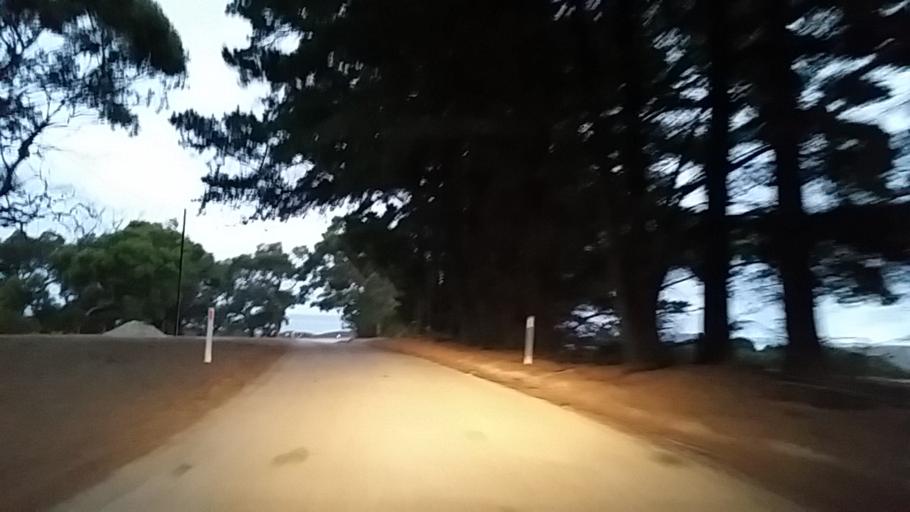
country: AU
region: South Australia
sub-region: Yankalilla
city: Normanville
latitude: -35.6312
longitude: 138.1932
